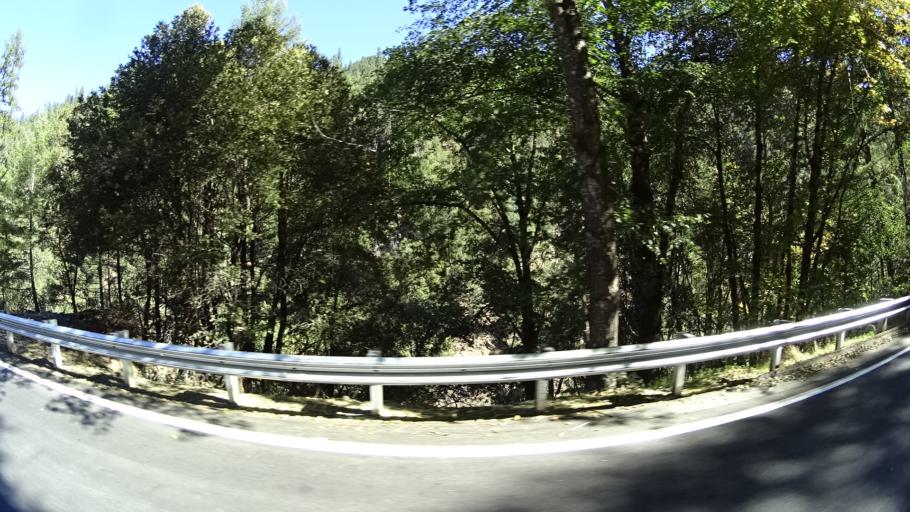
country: US
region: California
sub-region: Siskiyou County
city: Happy Camp
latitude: 41.3574
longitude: -123.4099
